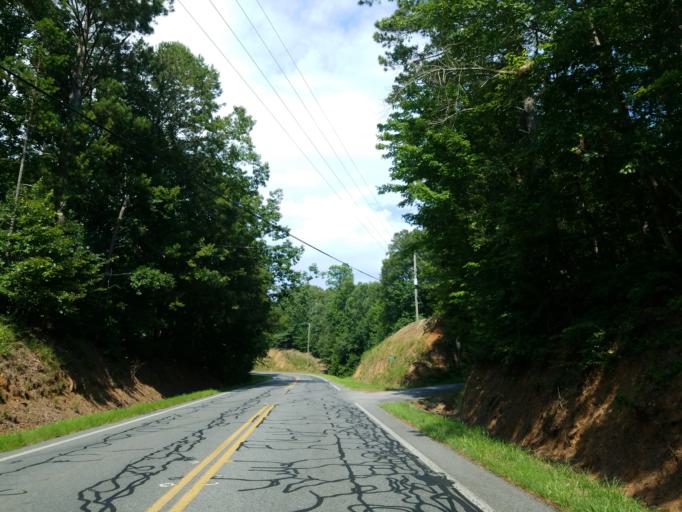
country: US
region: Georgia
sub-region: Gilmer County
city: Ellijay
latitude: 34.5888
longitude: -84.5959
